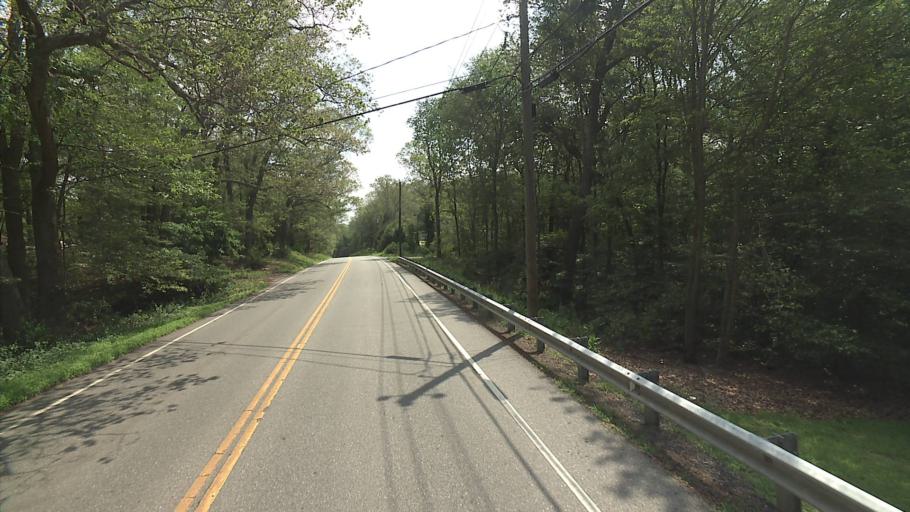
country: US
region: Connecticut
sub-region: New London County
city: Preston City
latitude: 41.5315
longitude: -71.9501
